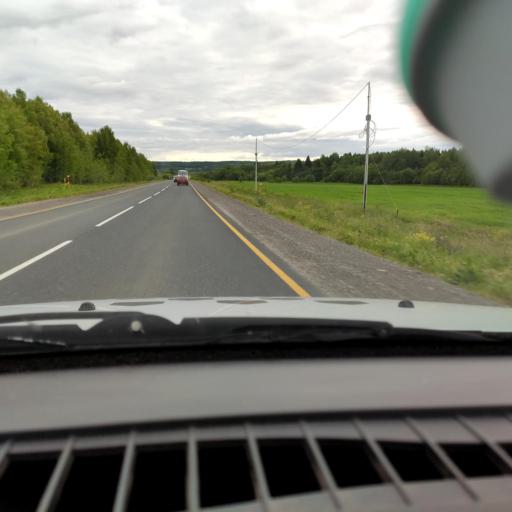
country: RU
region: Perm
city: Lys'va
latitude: 58.1746
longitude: 57.7843
